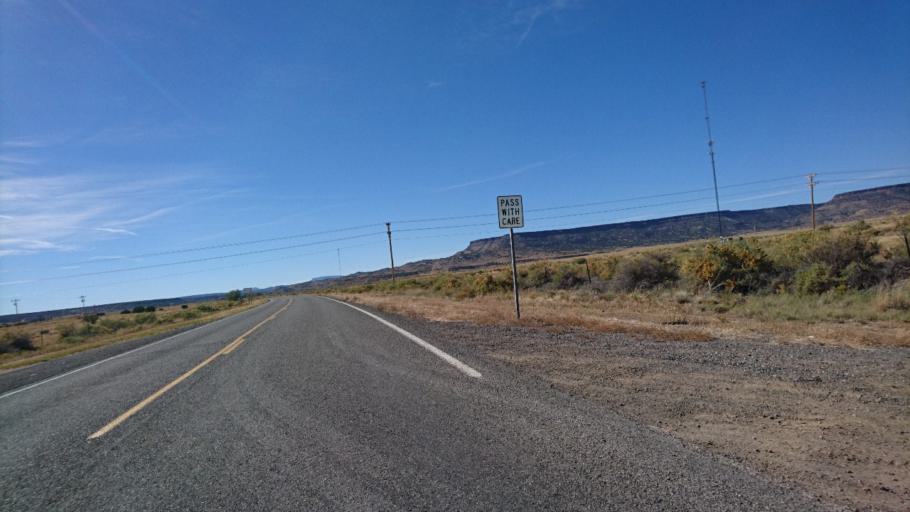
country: US
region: New Mexico
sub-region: Cibola County
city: Skyline-Ganipa
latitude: 35.0820
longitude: -107.6300
